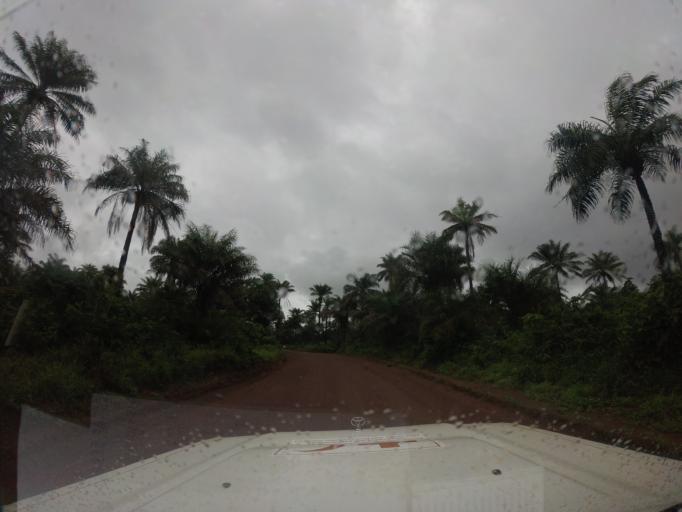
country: SL
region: Northern Province
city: Kambia
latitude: 9.1324
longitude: -12.8836
